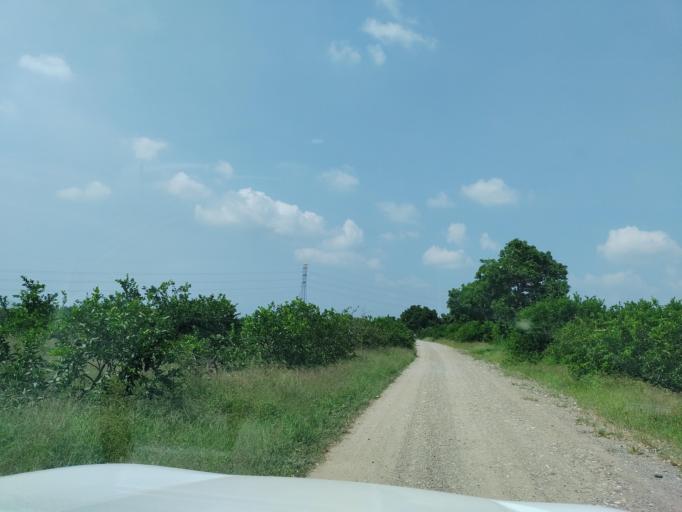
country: MX
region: Veracruz
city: Martinez de la Torre
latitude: 20.0895
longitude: -97.0519
